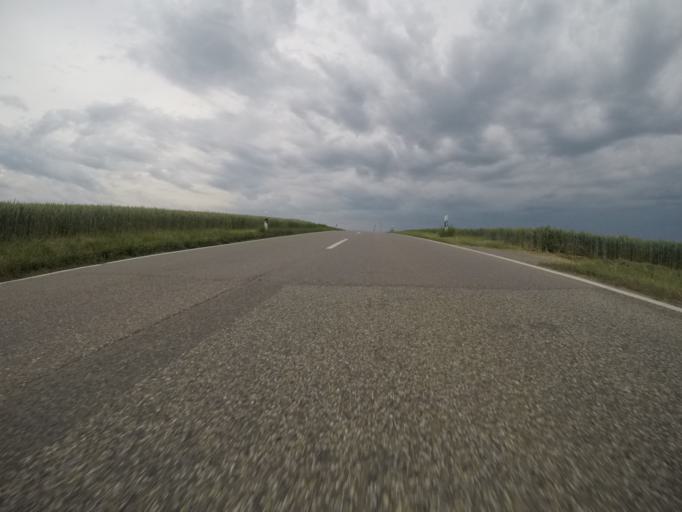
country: DE
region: Baden-Wuerttemberg
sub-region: Regierungsbezirk Stuttgart
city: Hemmingen
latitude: 48.8712
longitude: 9.0499
